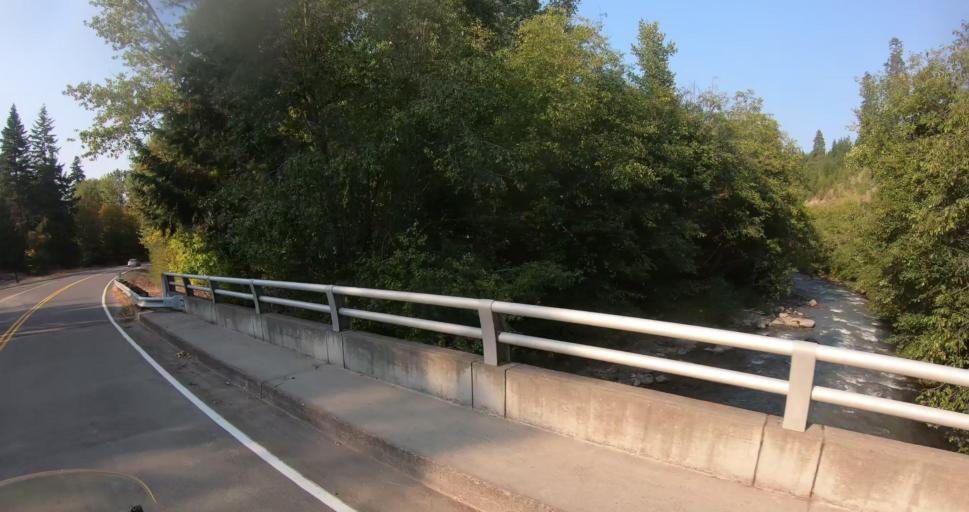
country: US
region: Oregon
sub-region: Hood River County
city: Odell
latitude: 45.4980
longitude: -121.5635
